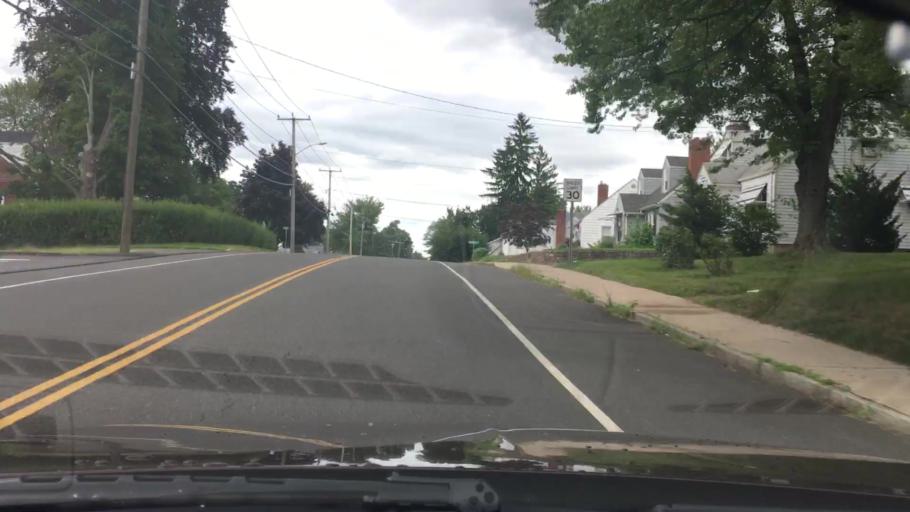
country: US
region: Connecticut
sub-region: Hartford County
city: Manchester
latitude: 41.7662
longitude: -72.5422
